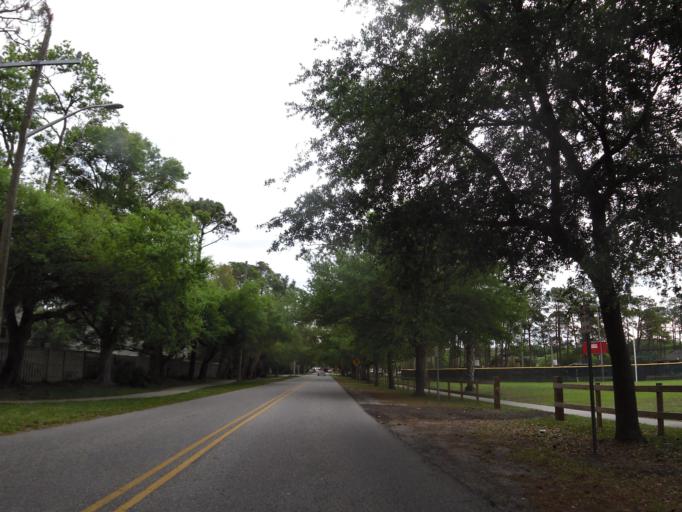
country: US
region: Florida
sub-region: Duval County
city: Atlantic Beach
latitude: 30.3327
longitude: -81.4054
